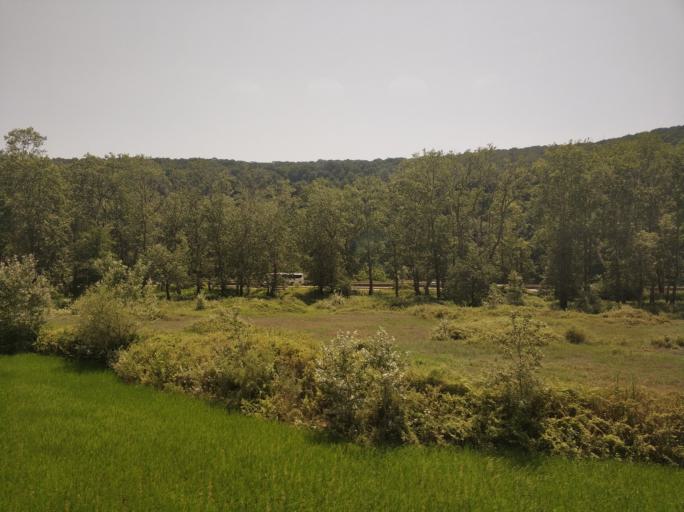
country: IR
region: Gilan
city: Pa'in-e Bazar-e Rudbar
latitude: 36.9575
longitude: 49.5521
